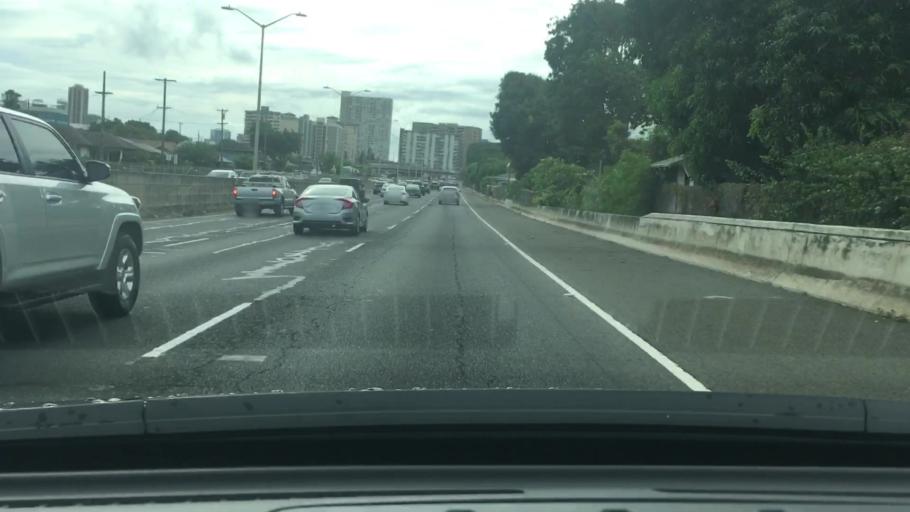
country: US
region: Hawaii
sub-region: Honolulu County
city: Honolulu
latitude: 21.2968
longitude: -157.8253
